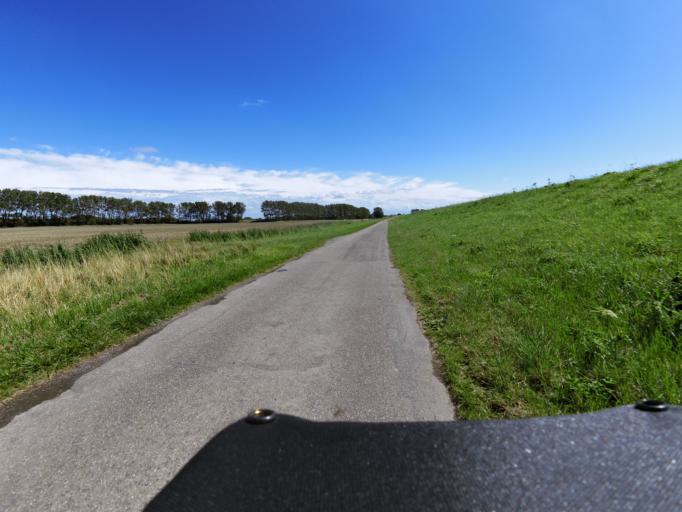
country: NL
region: South Holland
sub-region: Gemeente Goeree-Overflakkee
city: Goedereede
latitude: 51.8286
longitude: 4.0077
